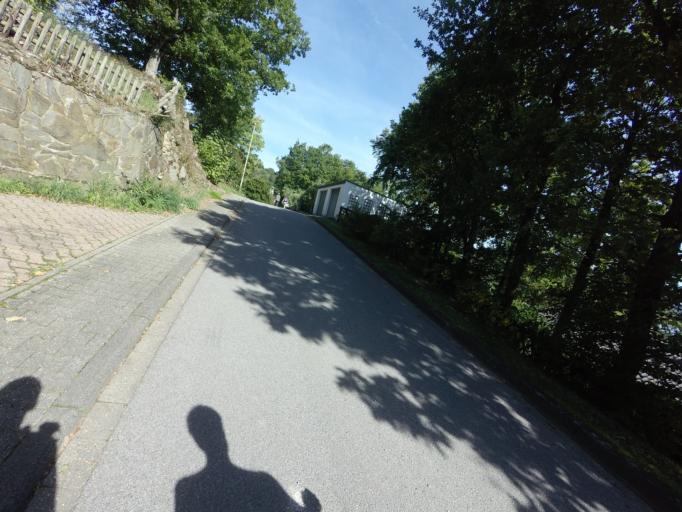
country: DE
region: North Rhine-Westphalia
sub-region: Regierungsbezirk Koln
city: Simmerath
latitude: 50.6208
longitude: 6.3801
